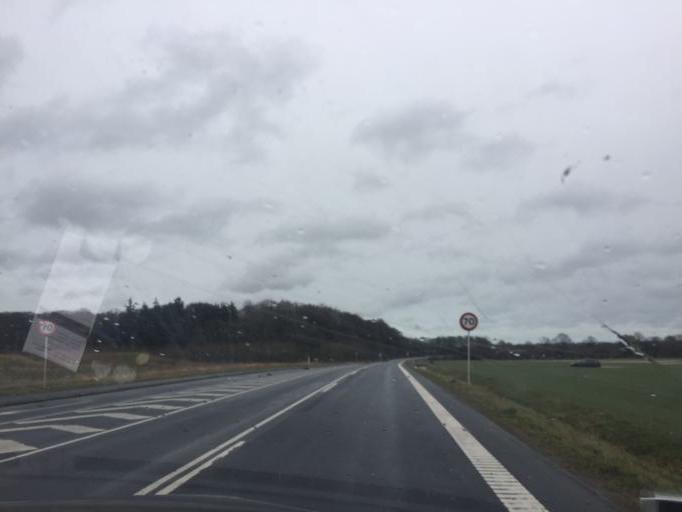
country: DK
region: South Denmark
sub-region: Fredericia Kommune
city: Snoghoj
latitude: 55.5344
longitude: 9.6694
